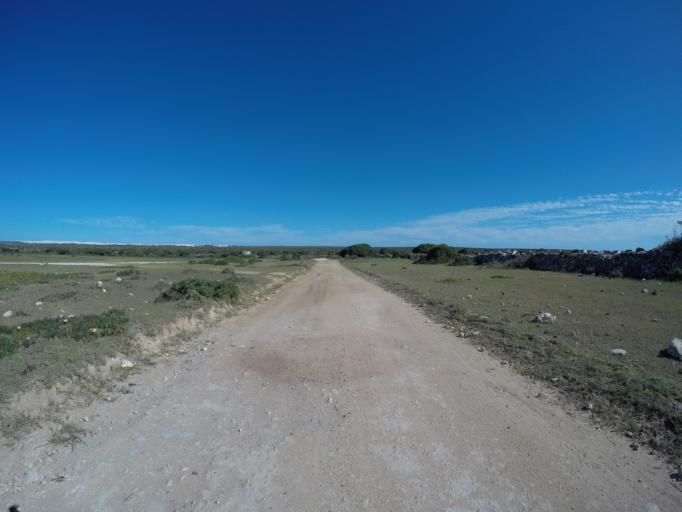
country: ZA
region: Western Cape
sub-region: Overberg District Municipality
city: Bredasdorp
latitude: -34.4539
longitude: 20.4093
